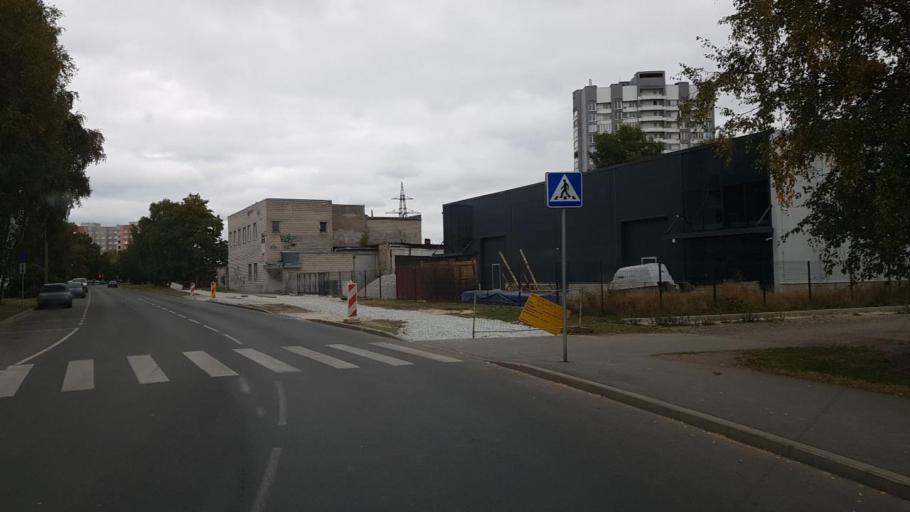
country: EE
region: Harju
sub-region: Tallinna linn
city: Tallinn
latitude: 59.4440
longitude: 24.6963
